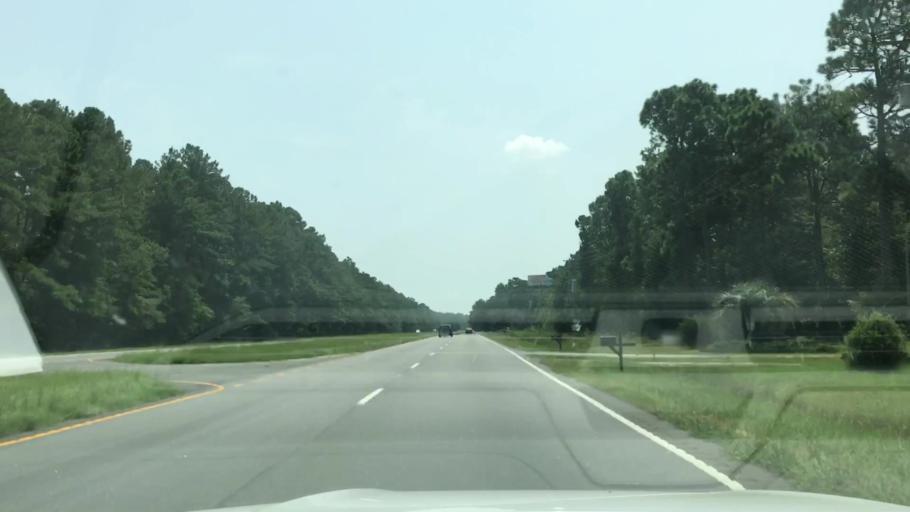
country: US
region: South Carolina
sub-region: Georgetown County
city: Georgetown
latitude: 33.2433
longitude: -79.3757
